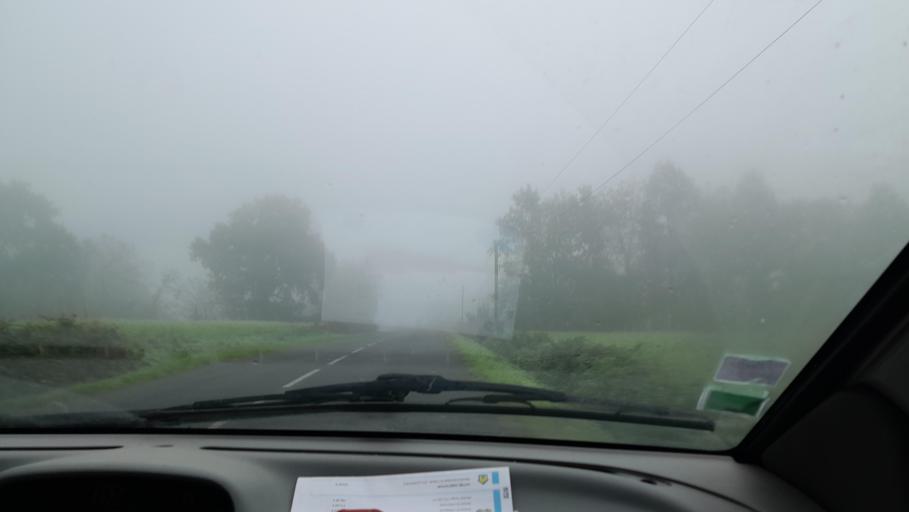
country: FR
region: Brittany
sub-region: Departement d'Ille-et-Vilaine
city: Le Pertre
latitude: 48.0664
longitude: -1.0252
